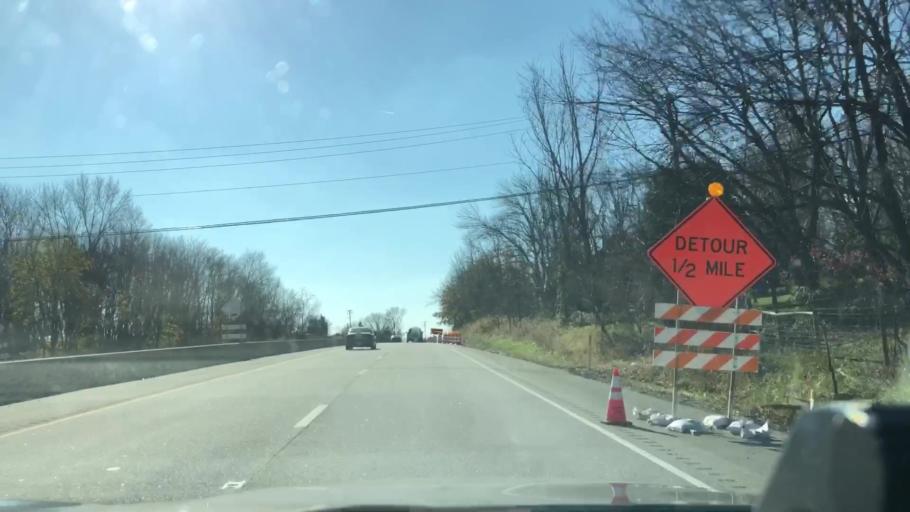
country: US
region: Pennsylvania
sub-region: Montgomery County
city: Halfway House
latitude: 40.2722
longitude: -75.6462
